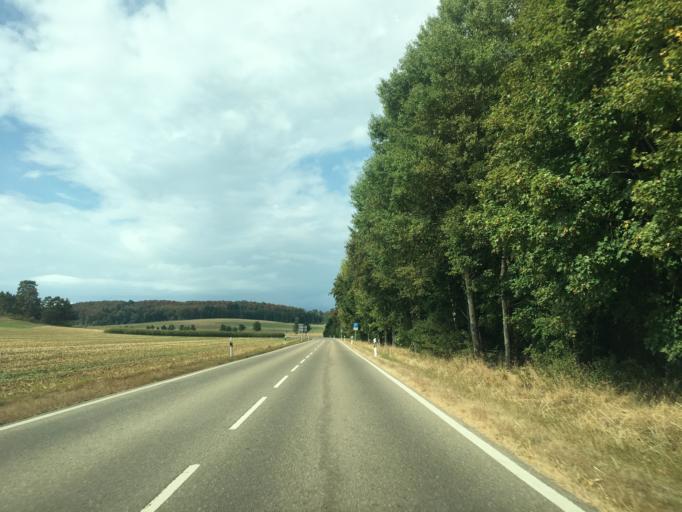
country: DE
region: Baden-Wuerttemberg
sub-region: Tuebingen Region
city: Trochtelfingen
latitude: 48.3647
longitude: 9.2529
